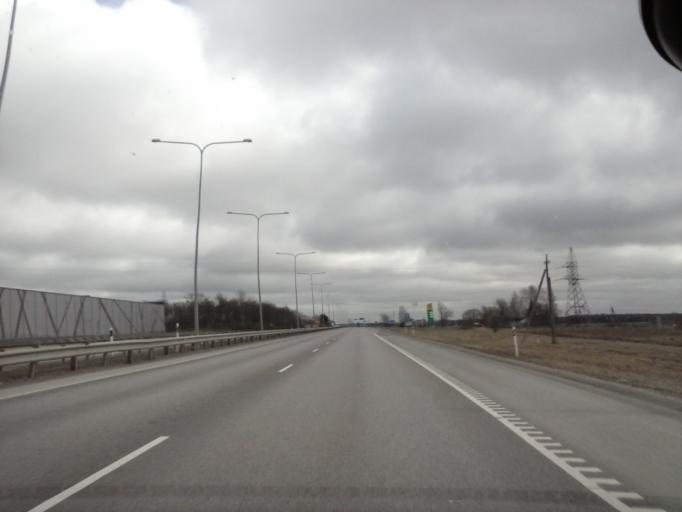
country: EE
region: Harju
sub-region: Rae vald
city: Jueri
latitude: 59.3629
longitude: 24.8673
